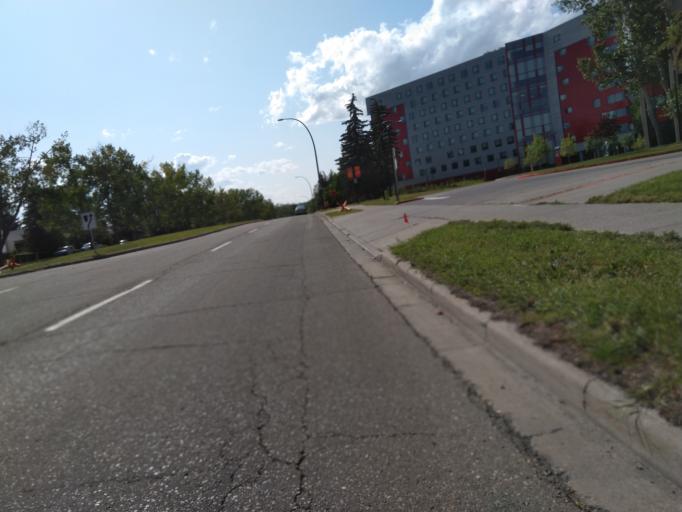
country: CA
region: Alberta
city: Calgary
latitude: 51.0745
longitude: -114.1323
